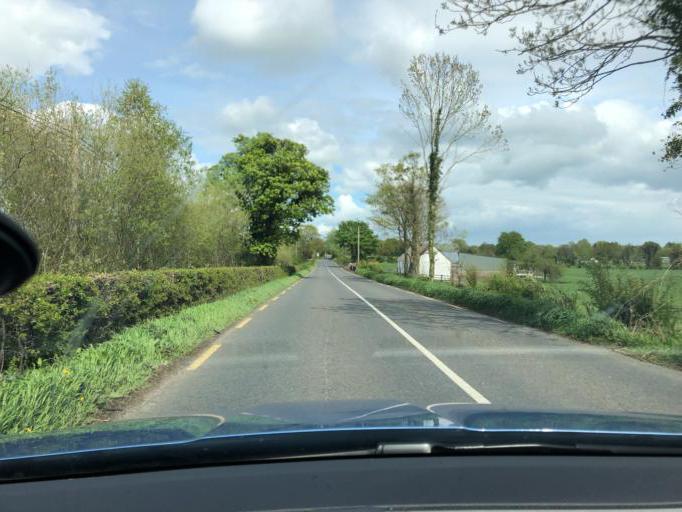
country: IE
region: Leinster
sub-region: Laois
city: Abbeyleix
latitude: 52.8957
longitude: -7.4151
